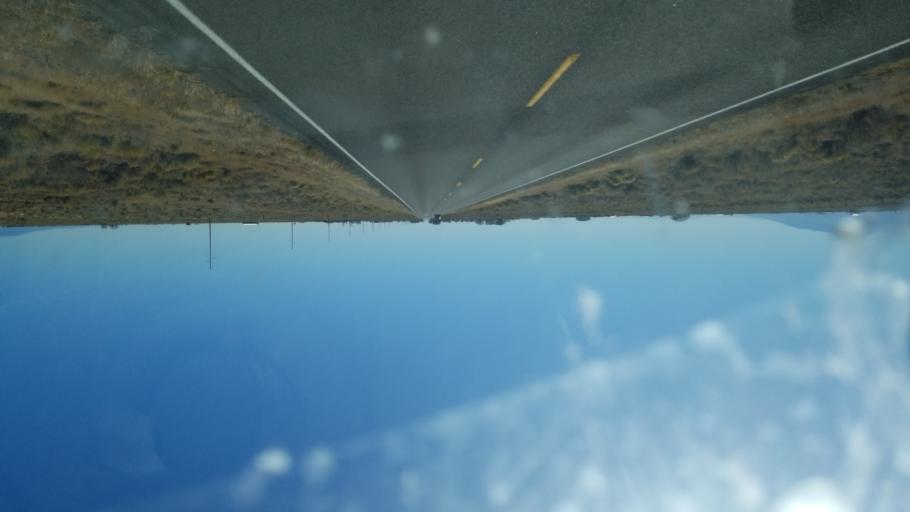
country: US
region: Colorado
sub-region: Saguache County
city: Saguache
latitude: 38.0368
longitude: -105.9127
